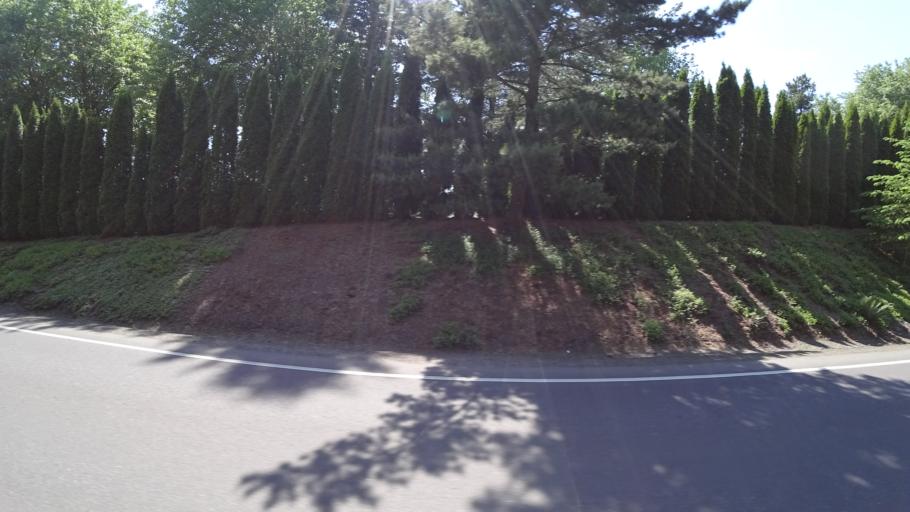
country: US
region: Oregon
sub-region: Washington County
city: Metzger
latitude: 45.4344
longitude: -122.7195
